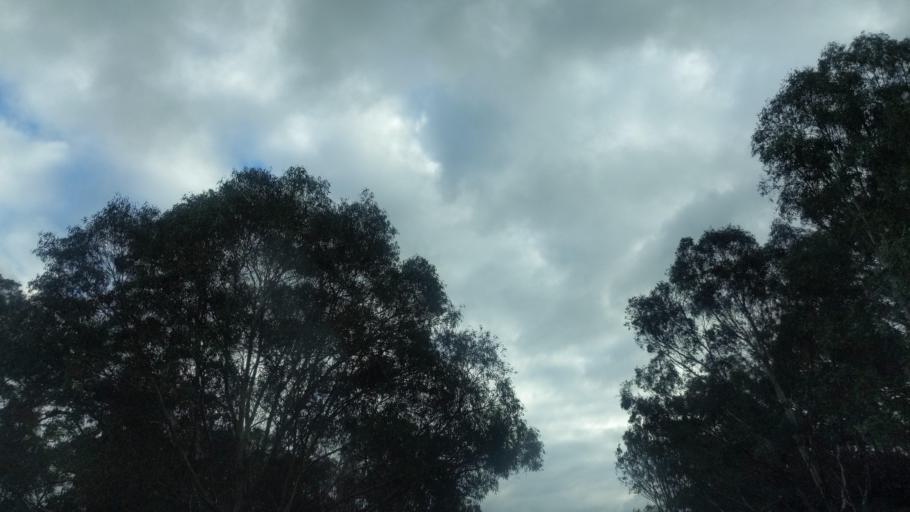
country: AU
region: New South Wales
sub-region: Wagga Wagga
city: Forest Hill
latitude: -35.1615
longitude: 147.5106
